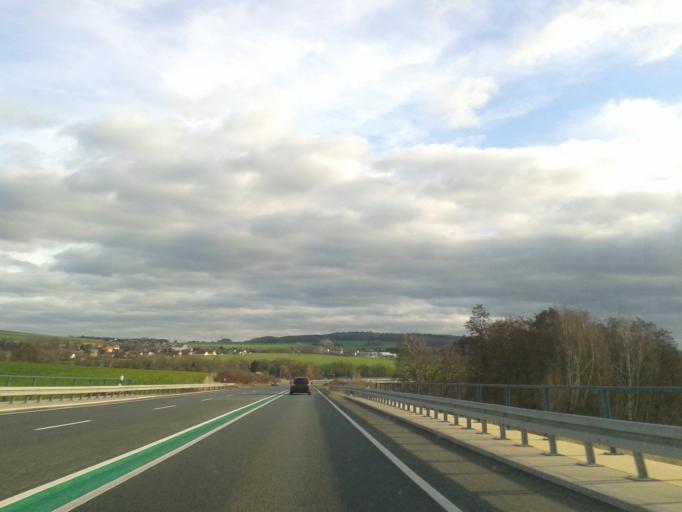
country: DE
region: Saxony
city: Lobau
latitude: 51.0793
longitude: 14.6590
